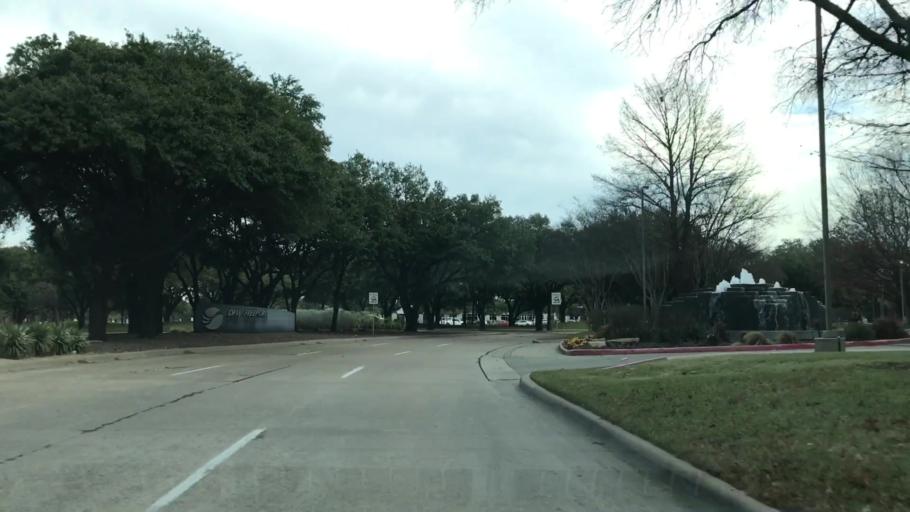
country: US
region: Texas
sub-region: Dallas County
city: Coppell
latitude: 32.9237
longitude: -97.0180
